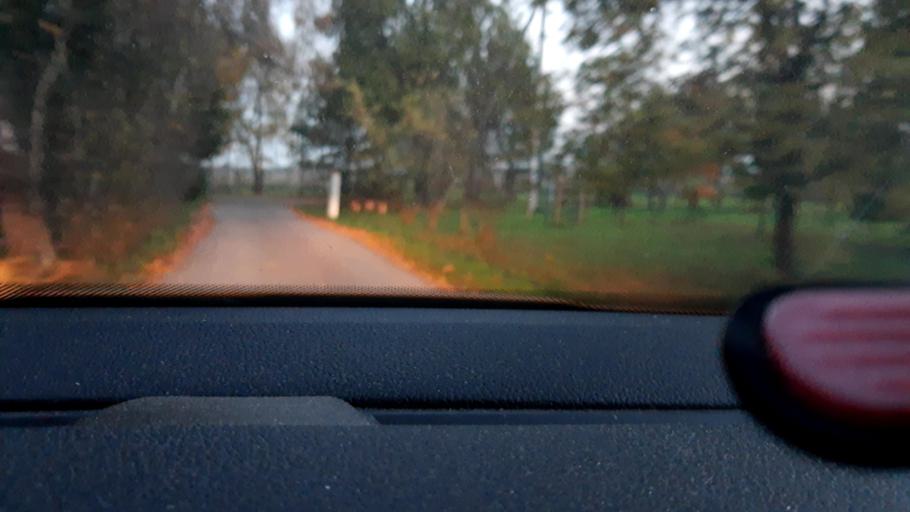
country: RU
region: Moskovskaya
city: Filimonki
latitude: 55.5362
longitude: 37.3580
